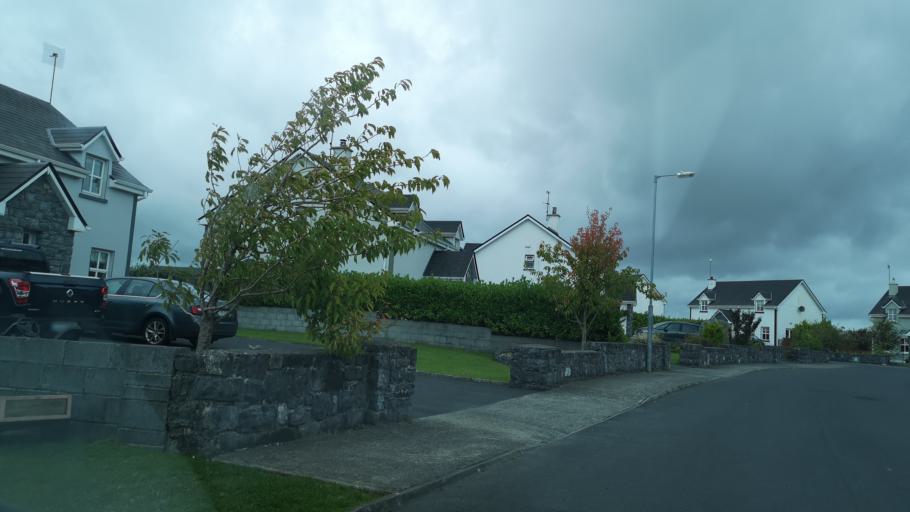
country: IE
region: Connaught
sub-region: County Galway
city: Athenry
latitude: 53.2760
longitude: -8.6400
